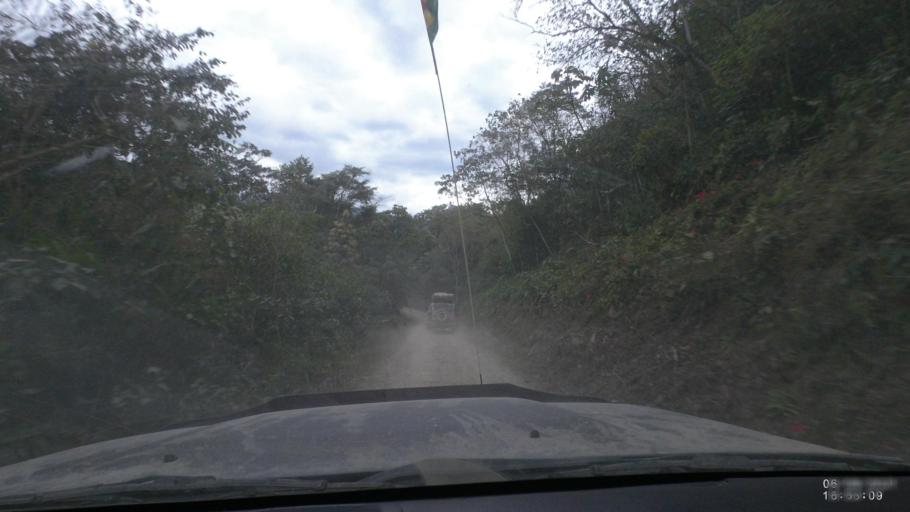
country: BO
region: La Paz
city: Quime
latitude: -16.4906
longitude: -66.7791
